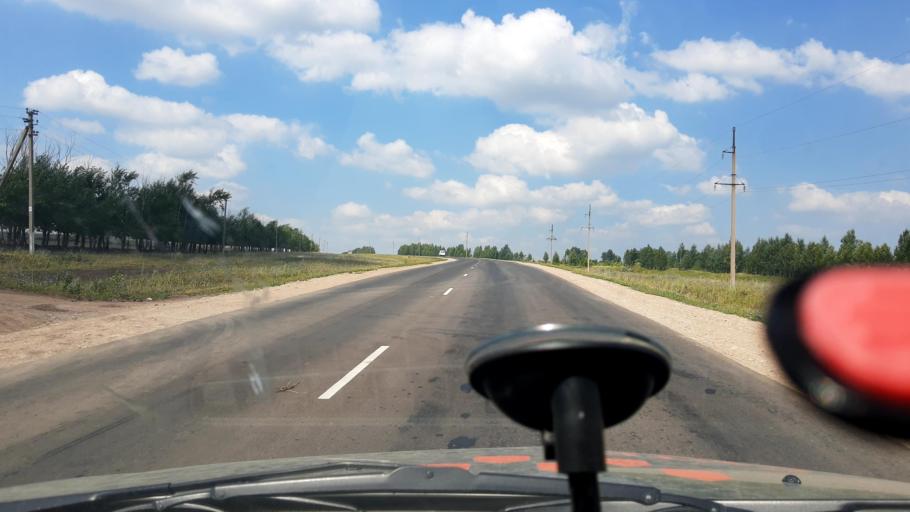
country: RU
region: Bashkortostan
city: Chekmagush
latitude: 54.9066
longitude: 54.5872
